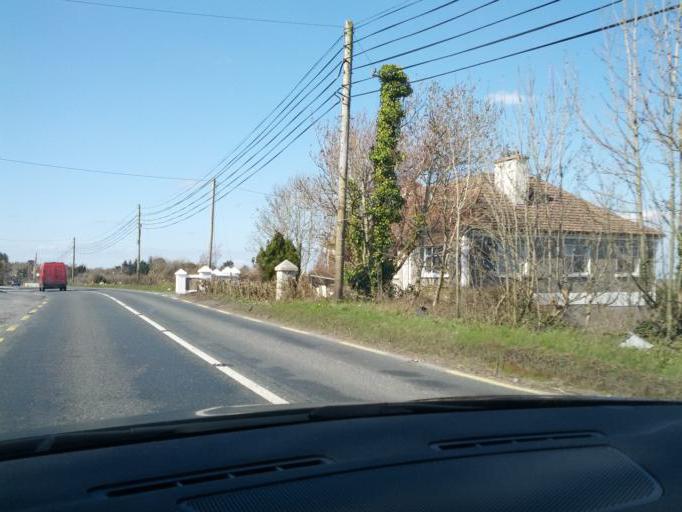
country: IE
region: Connaught
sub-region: County Galway
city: Moycullen
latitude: 53.3238
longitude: -9.1642
